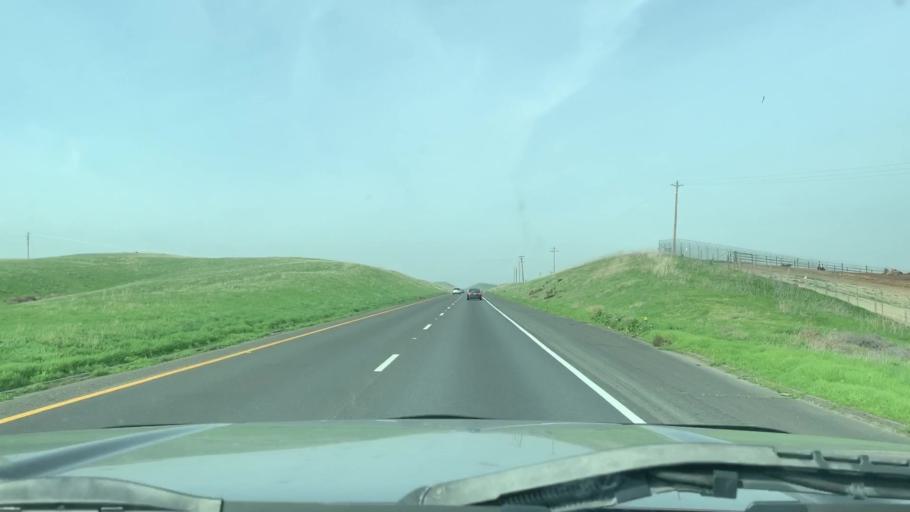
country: US
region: California
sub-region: Fresno County
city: Coalinga
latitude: 36.3092
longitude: -120.2805
